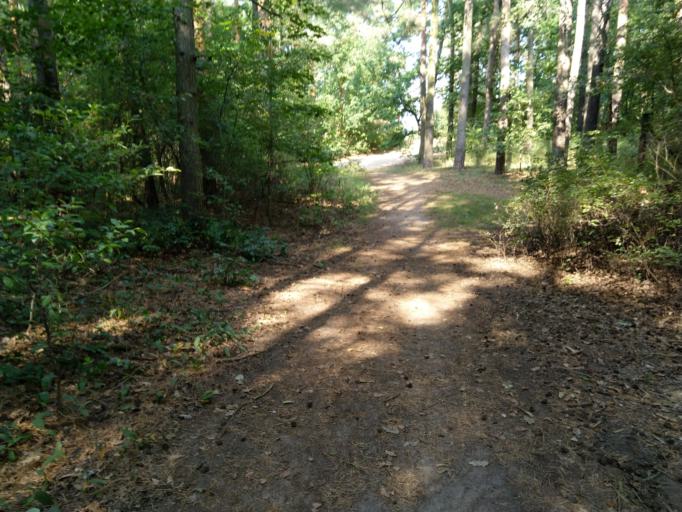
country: DE
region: Brandenburg
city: Woltersdorf
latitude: 52.4478
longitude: 13.7466
